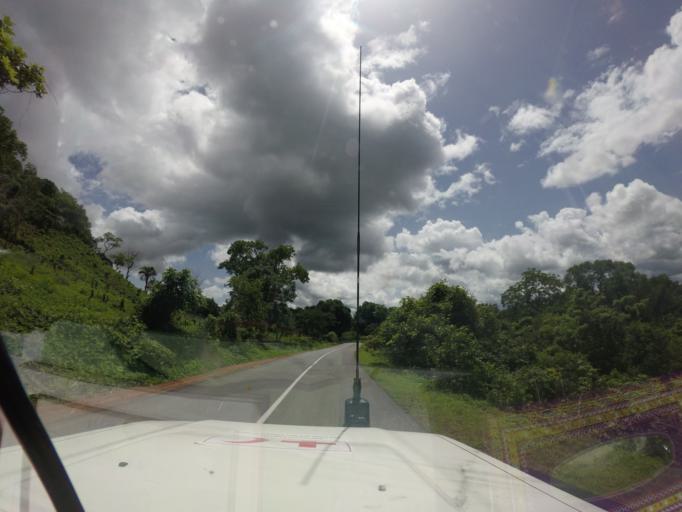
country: SL
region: Northern Province
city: Bindi
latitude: 10.1648
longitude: -11.5093
